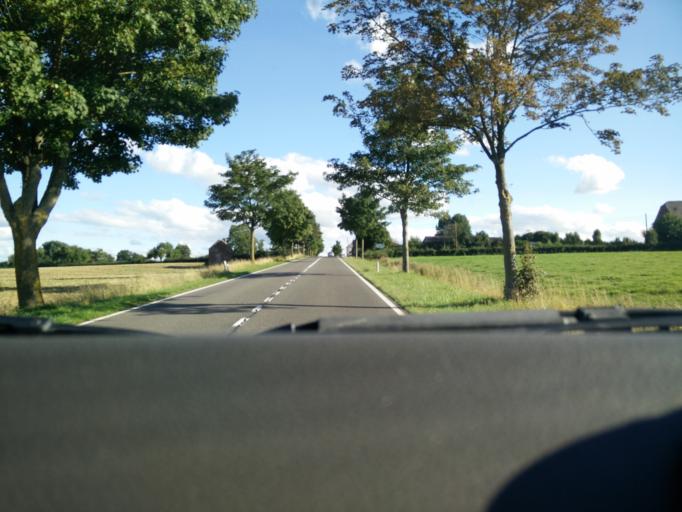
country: BE
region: Wallonia
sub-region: Province du Hainaut
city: Beaumont
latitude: 50.2653
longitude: 4.2172
